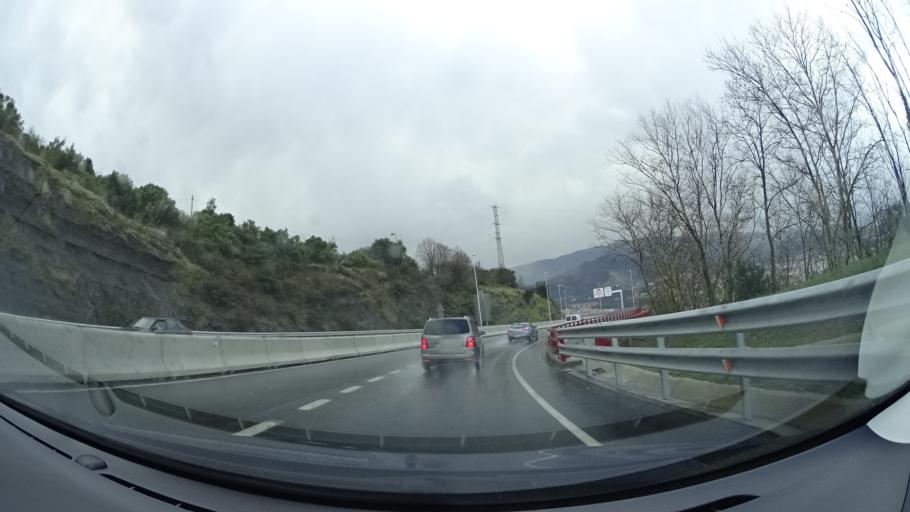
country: ES
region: Basque Country
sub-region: Bizkaia
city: Santutxu
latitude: 43.2669
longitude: -2.9073
